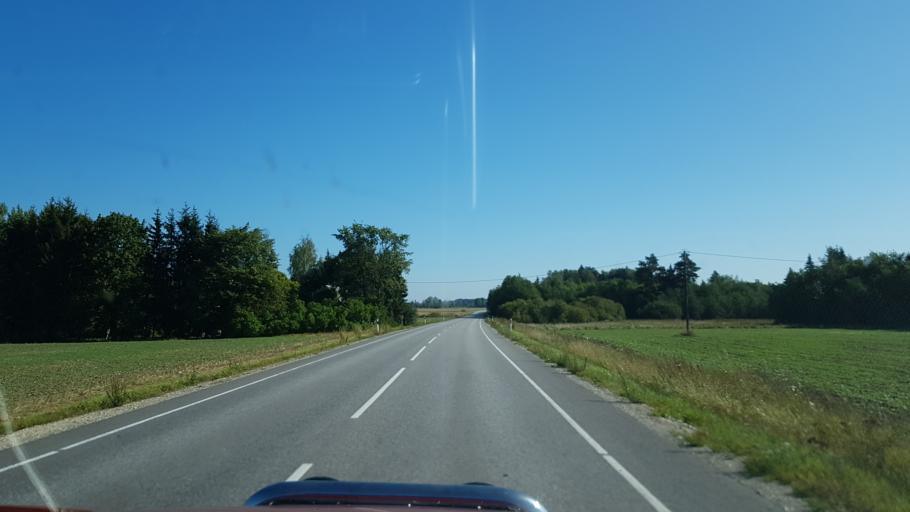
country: EE
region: Jogevamaa
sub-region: Tabivere vald
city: Tabivere
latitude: 58.4596
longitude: 26.5388
